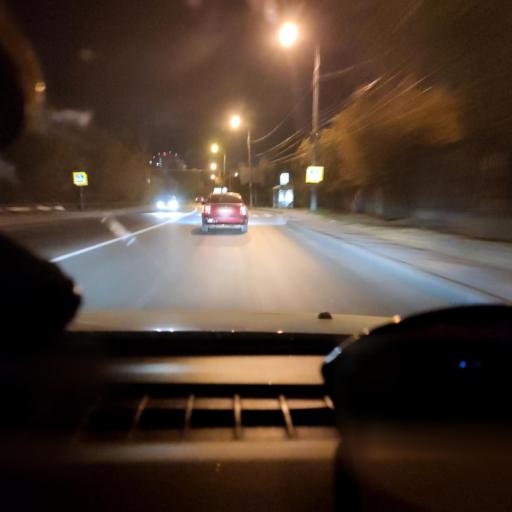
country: RU
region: Samara
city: Rozhdestveno
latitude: 53.1615
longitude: 50.0759
